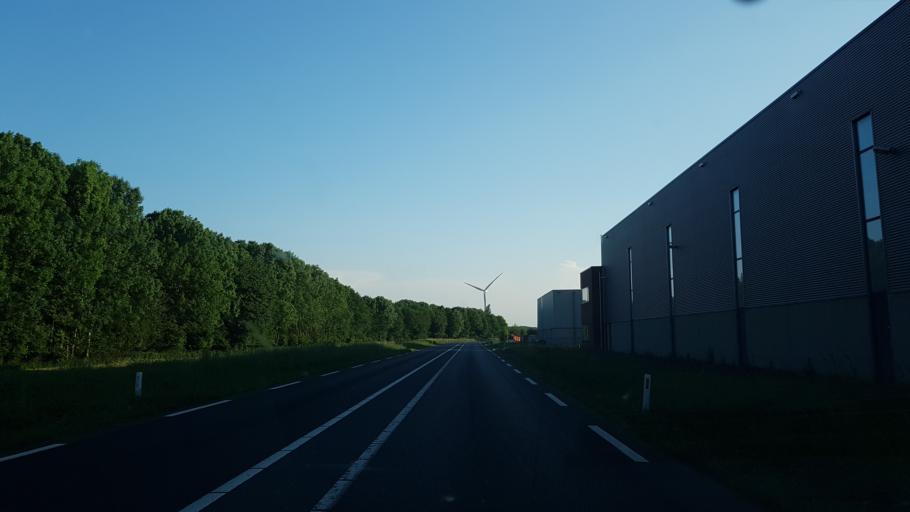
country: NL
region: Gelderland
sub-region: Gemeente Montferland
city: s-Heerenberg
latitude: 51.8719
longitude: 6.2669
